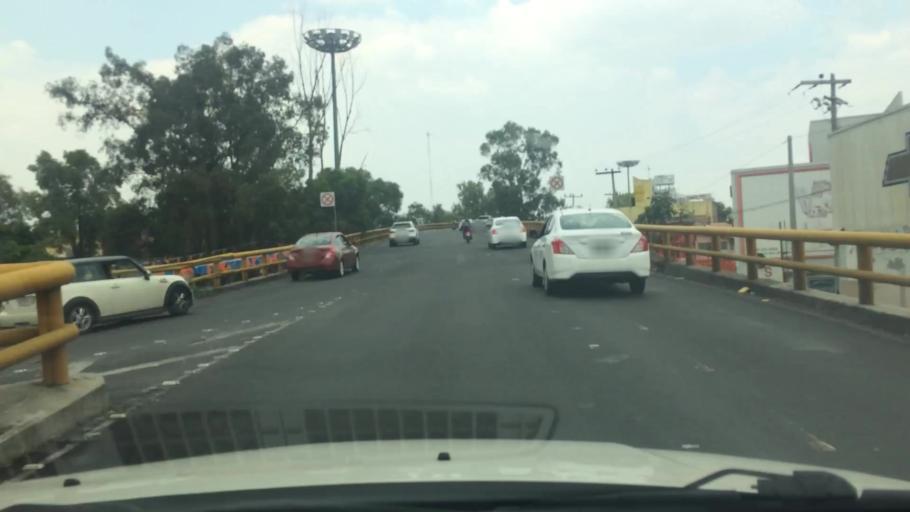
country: MX
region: Mexico City
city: Tlalpan
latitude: 19.3173
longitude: -99.1379
